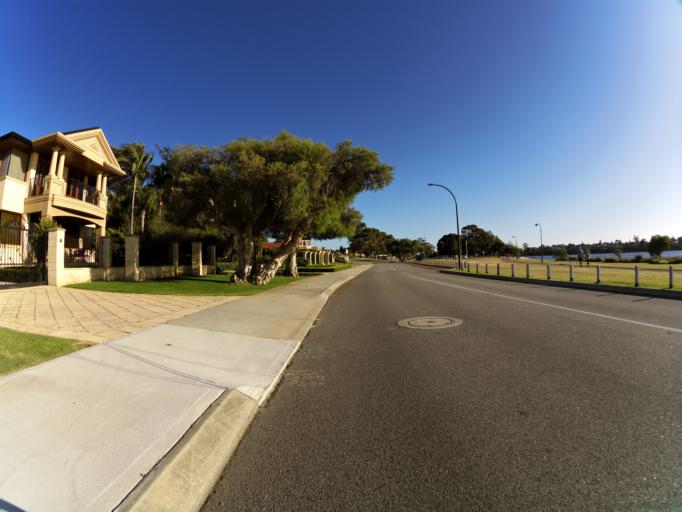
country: AU
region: Western Australia
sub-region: Melville
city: Mount Pleasant
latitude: -32.0268
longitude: 115.8522
